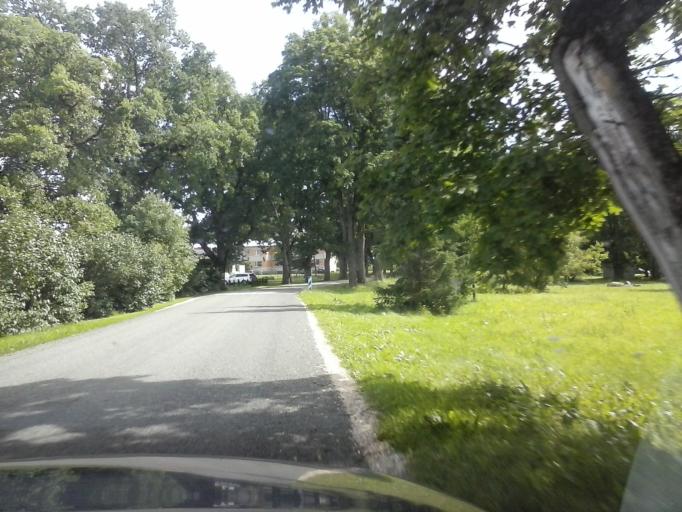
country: EE
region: Laeaene-Virumaa
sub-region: Vaeike-Maarja vald
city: Vaike-Maarja
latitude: 59.0792
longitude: 26.1958
